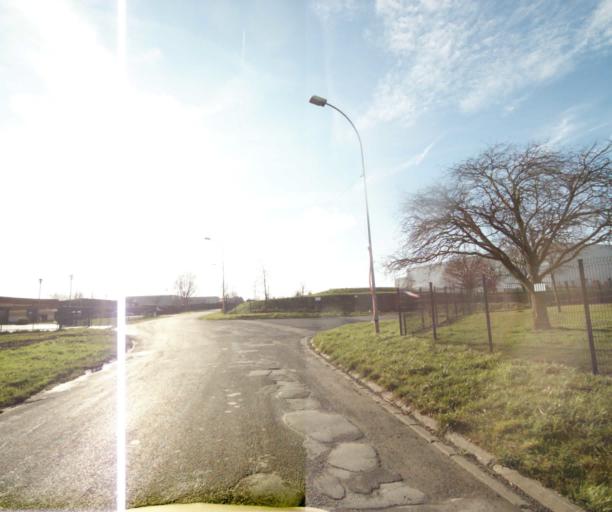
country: FR
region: Nord-Pas-de-Calais
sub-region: Departement du Nord
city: Saultain
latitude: 50.3471
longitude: 3.5663
